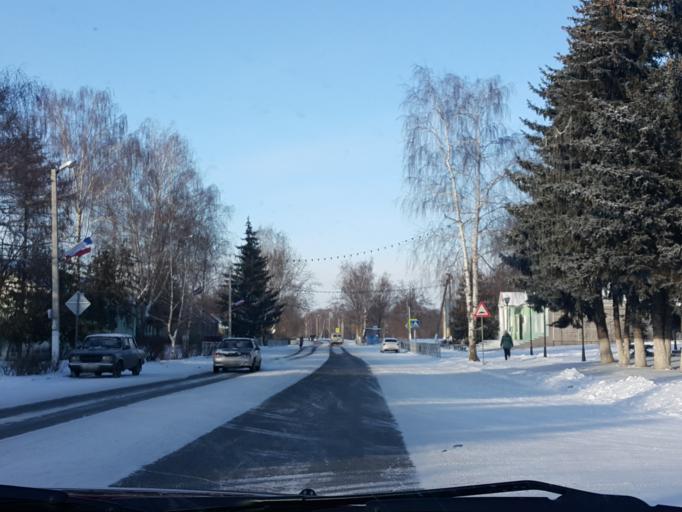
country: RU
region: Tambov
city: Znamenka
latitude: 52.4158
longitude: 41.4406
